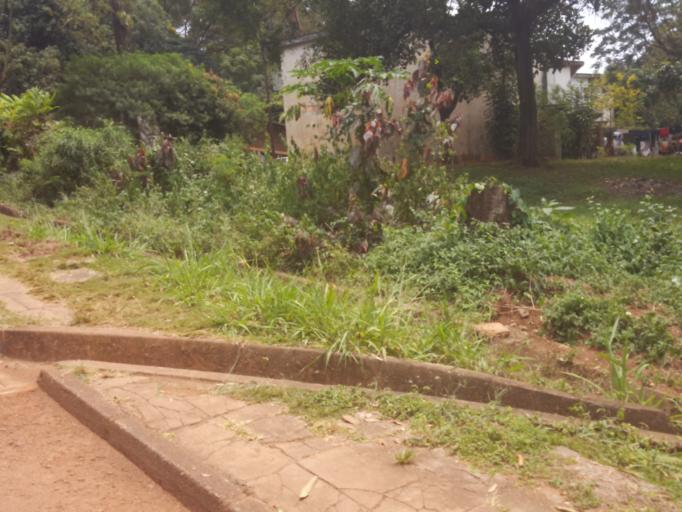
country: UG
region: Central Region
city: Kampala Central Division
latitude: 0.3382
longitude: 32.5669
